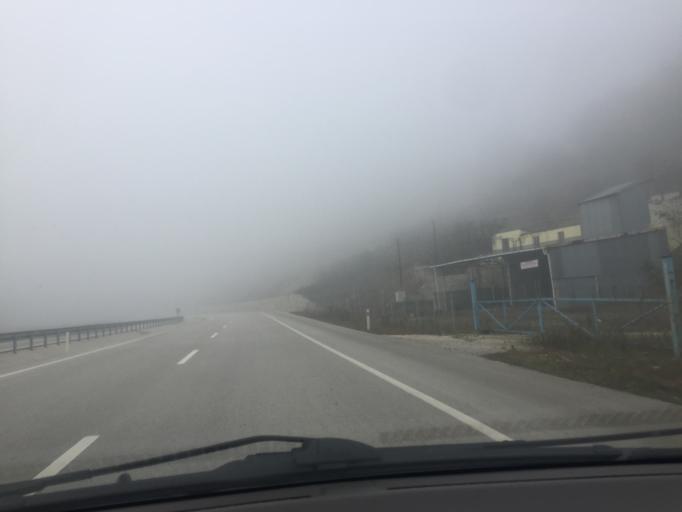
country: TR
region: Canakkale
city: Can
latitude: 40.0932
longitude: 27.1564
